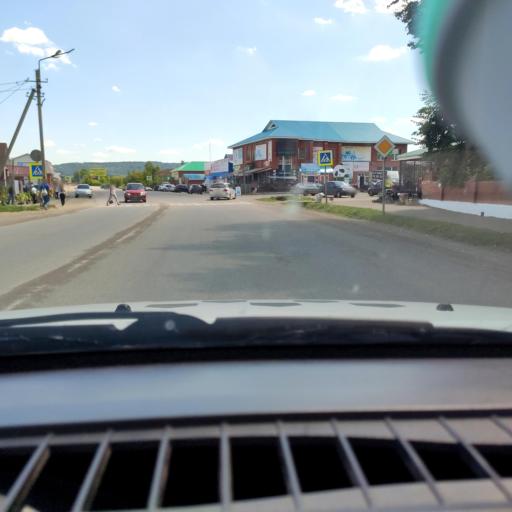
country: RU
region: Bashkortostan
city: Mesyagutovo
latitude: 55.5326
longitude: 58.2488
